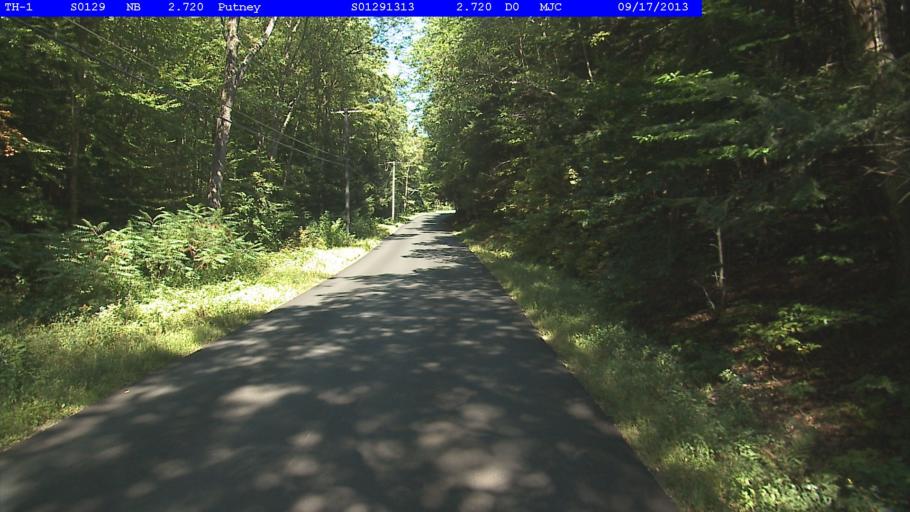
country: US
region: New Hampshire
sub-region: Cheshire County
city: Westmoreland
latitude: 43.0113
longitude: -72.5288
